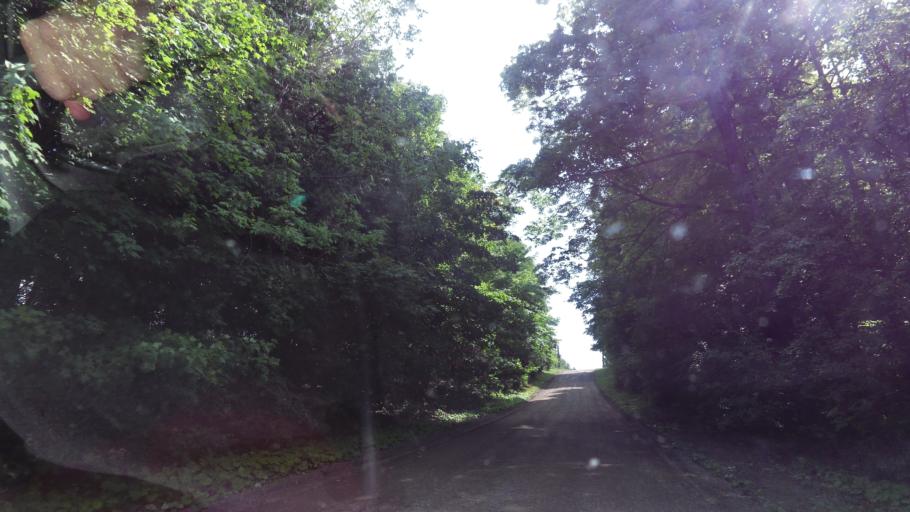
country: CA
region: Ontario
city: Oshawa
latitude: 44.0036
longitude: -78.8775
